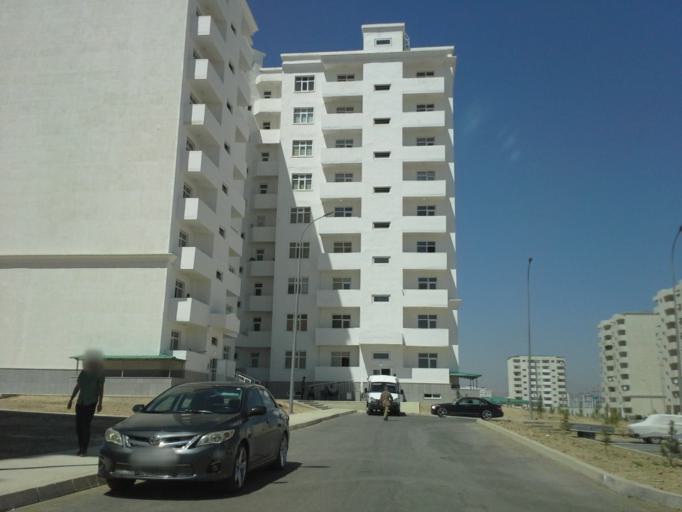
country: TM
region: Ahal
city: Ashgabat
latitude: 37.8859
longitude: 58.4107
